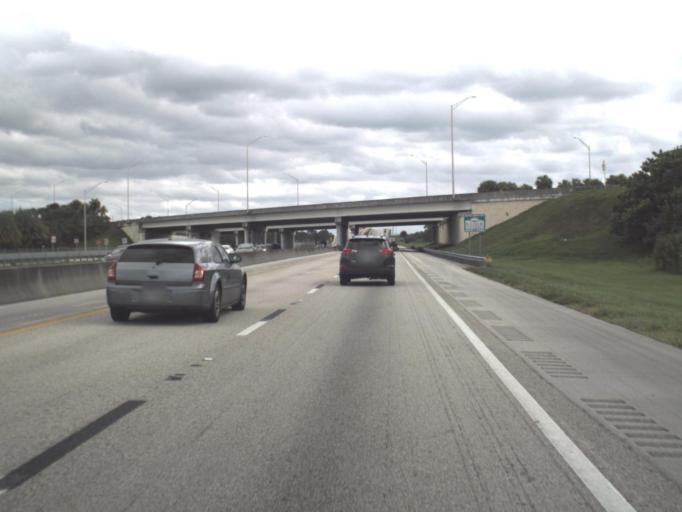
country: US
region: Florida
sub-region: Martin County
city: Palm City
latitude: 27.1267
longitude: -80.2812
